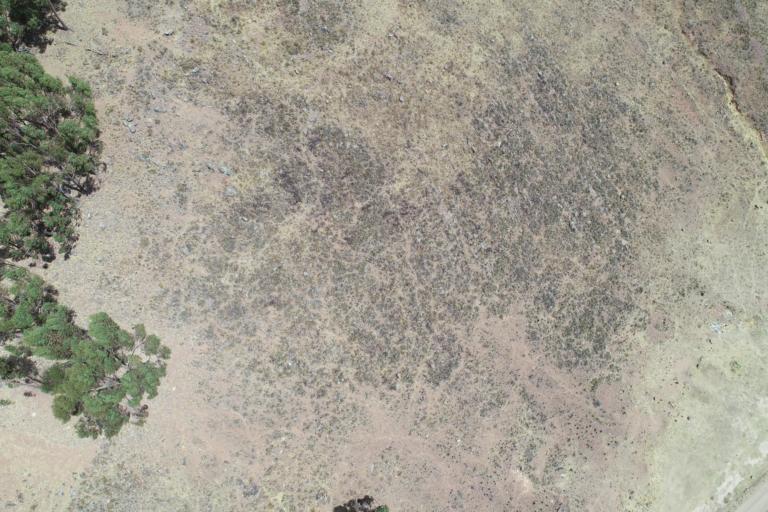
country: BO
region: La Paz
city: Achacachi
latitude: -15.9103
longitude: -68.8847
